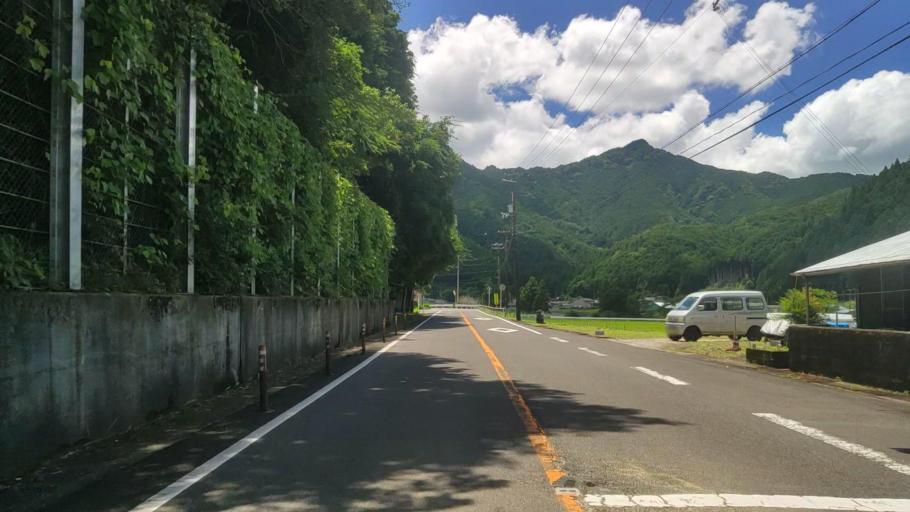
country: JP
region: Mie
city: Owase
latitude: 33.9819
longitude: 136.0491
